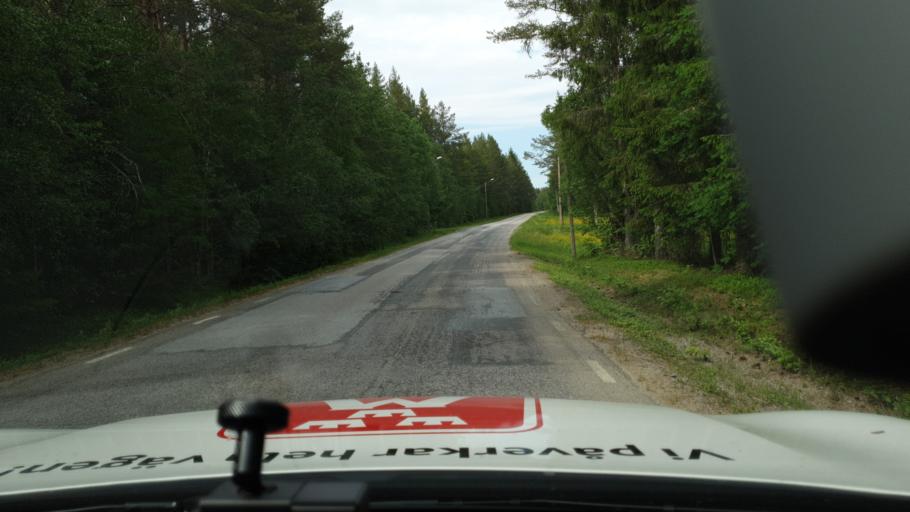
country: SE
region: Vaesterbotten
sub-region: Nordmalings Kommun
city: Nordmaling
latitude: 63.5480
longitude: 19.7024
